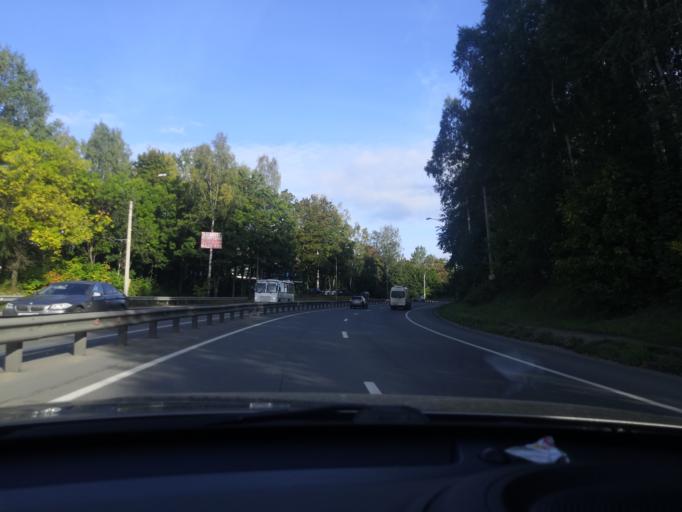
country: RU
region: St.-Petersburg
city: Pargolovo
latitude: 60.0804
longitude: 30.2642
